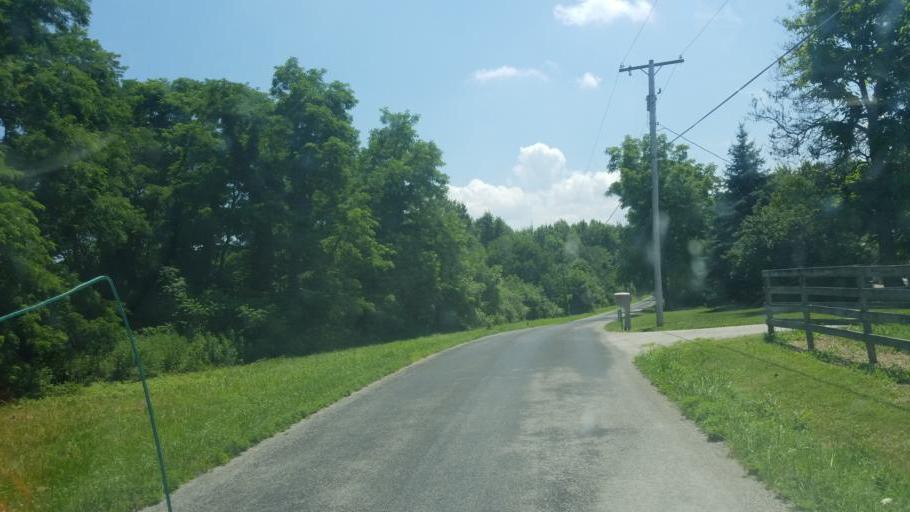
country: US
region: Ohio
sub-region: Richland County
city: Ontario
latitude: 40.8385
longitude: -82.5942
